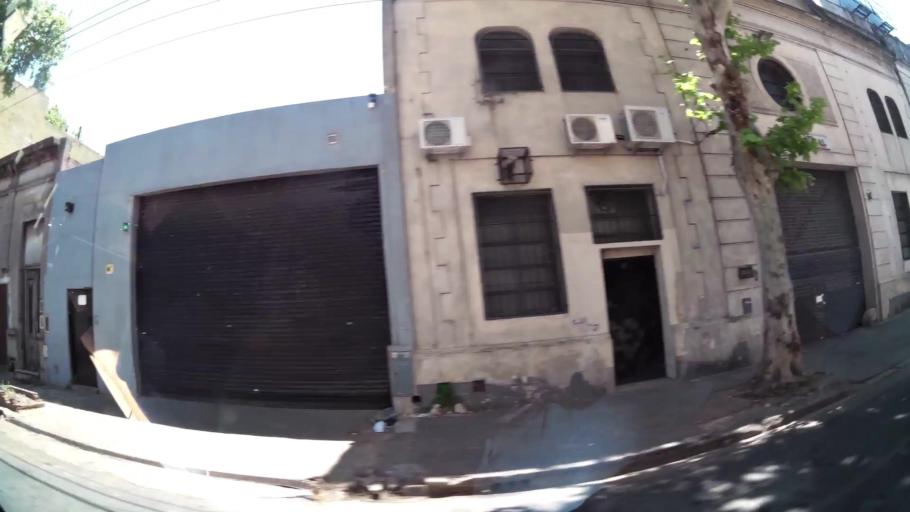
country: AR
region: Buenos Aires
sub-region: Partido de Avellaneda
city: Avellaneda
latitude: -34.6535
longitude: -58.3808
